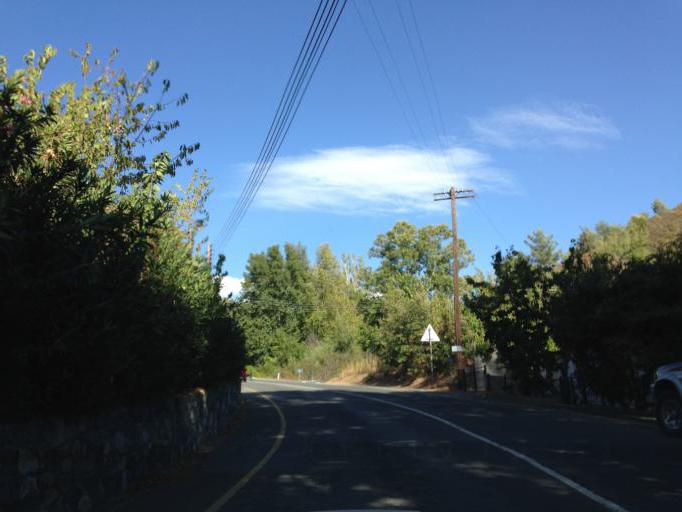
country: CY
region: Limassol
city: Pachna
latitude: 34.8797
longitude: 32.8423
